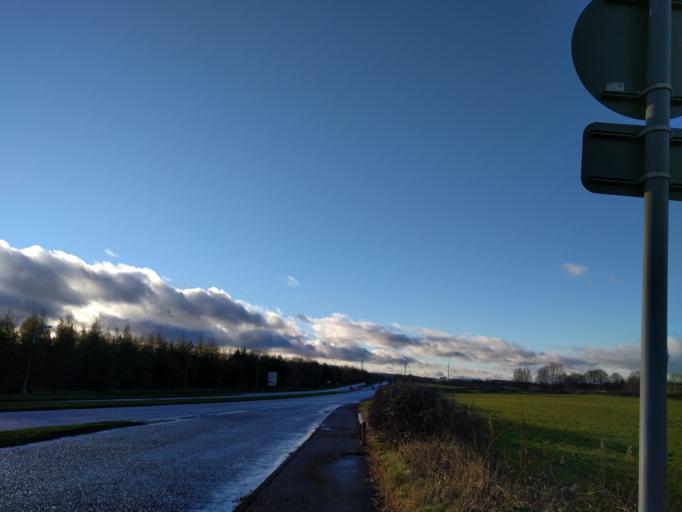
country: GB
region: England
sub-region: Northumberland
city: Cramlington
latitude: 55.1040
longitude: -1.5762
